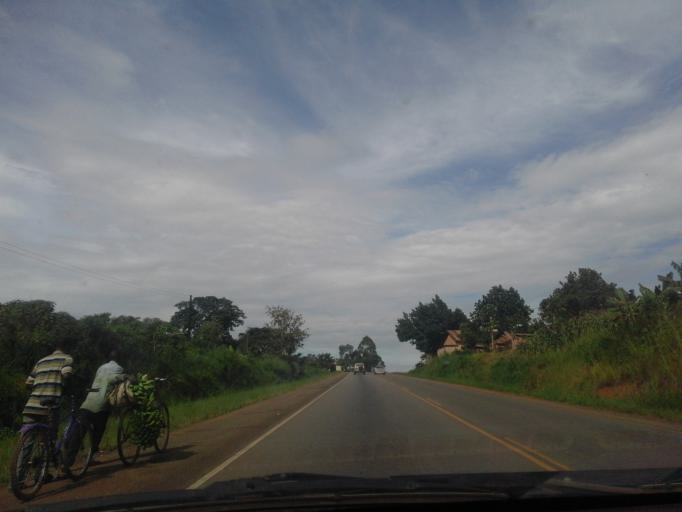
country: UG
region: Central Region
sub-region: Lwengo District
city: Lwengo
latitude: -0.3574
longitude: 31.5458
